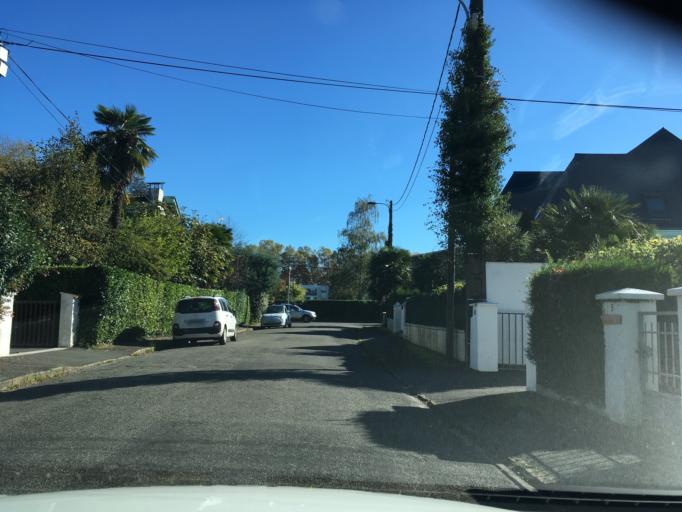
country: FR
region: Aquitaine
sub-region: Departement des Pyrenees-Atlantiques
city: Bizanos
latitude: 43.3031
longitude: -0.3449
